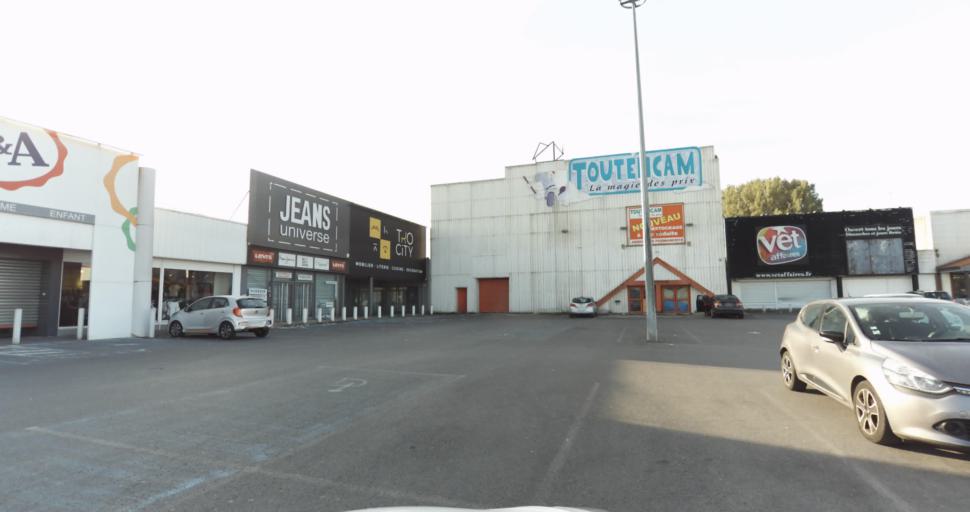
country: FR
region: Champagne-Ardenne
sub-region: Departement des Ardennes
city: Villers-Semeuse
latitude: 49.7323
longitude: 4.7556
